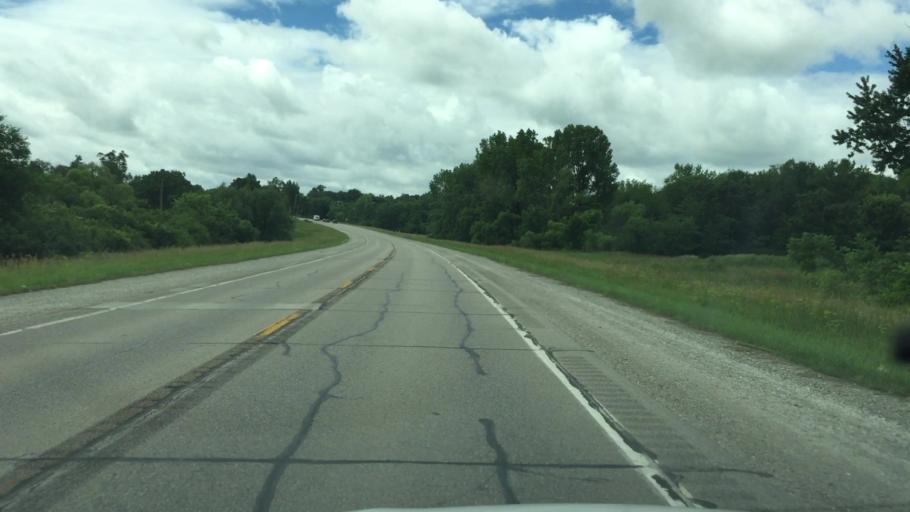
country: US
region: Iowa
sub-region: Jasper County
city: Monroe
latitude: 41.5366
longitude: -93.1011
